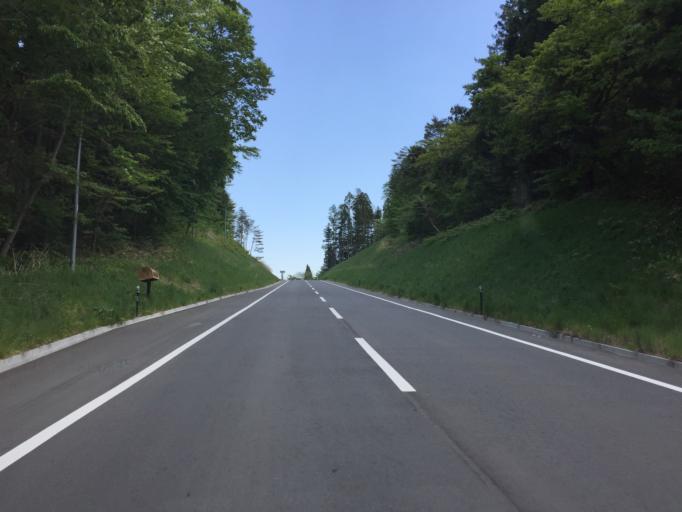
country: JP
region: Fukushima
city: Funehikimachi-funehiki
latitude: 37.5113
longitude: 140.6963
